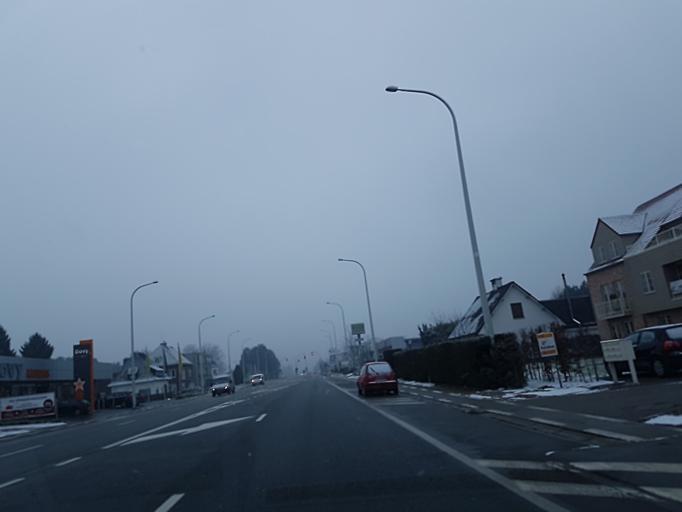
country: BE
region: Flanders
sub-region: Provincie Oost-Vlaanderen
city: Sint-Niklaas
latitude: 51.1738
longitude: 4.1858
